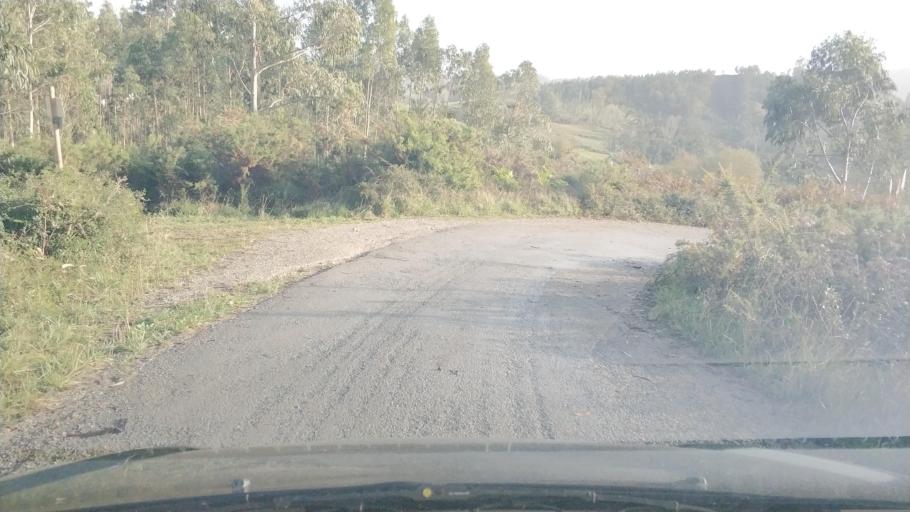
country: ES
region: Cantabria
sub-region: Provincia de Cantabria
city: Luzmela
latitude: 43.3388
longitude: -4.1888
